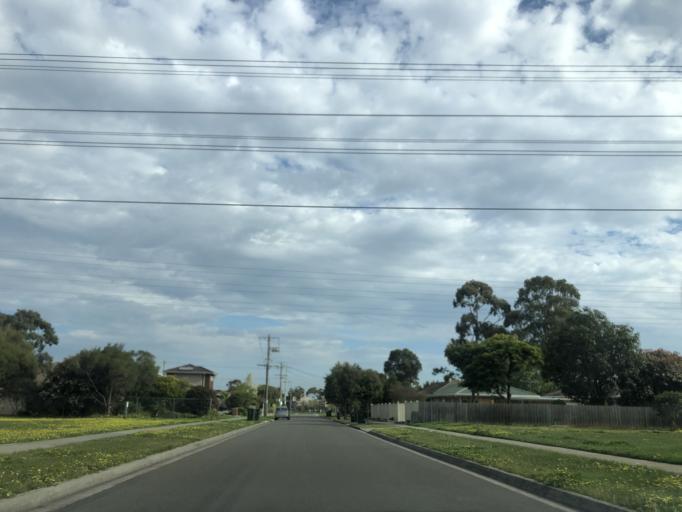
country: AU
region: Victoria
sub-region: Monash
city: Notting Hill
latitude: -37.8930
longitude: 145.1493
